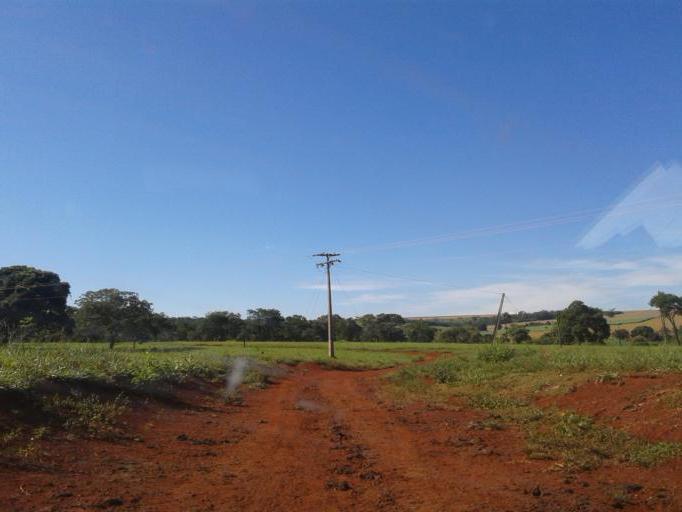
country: BR
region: Minas Gerais
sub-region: Capinopolis
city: Capinopolis
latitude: -18.6699
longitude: -49.6366
